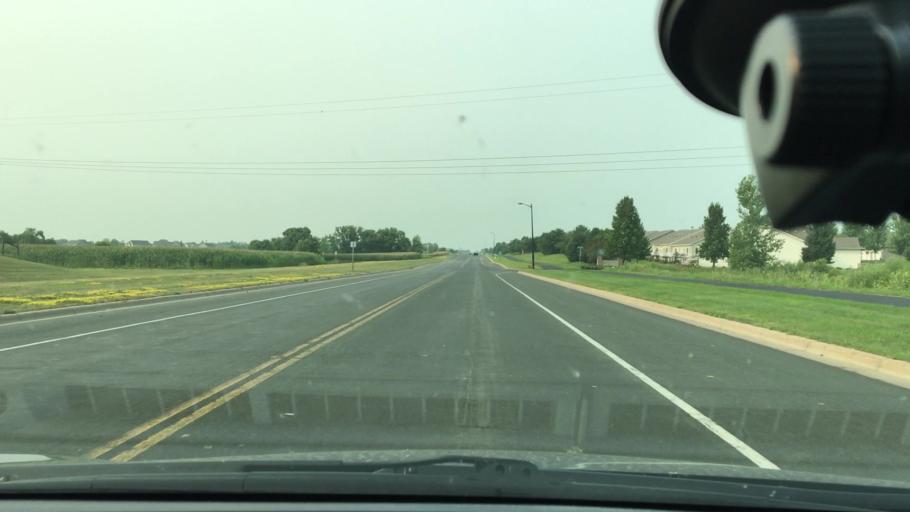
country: US
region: Minnesota
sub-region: Wright County
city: Albertville
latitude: 45.2423
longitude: -93.6427
